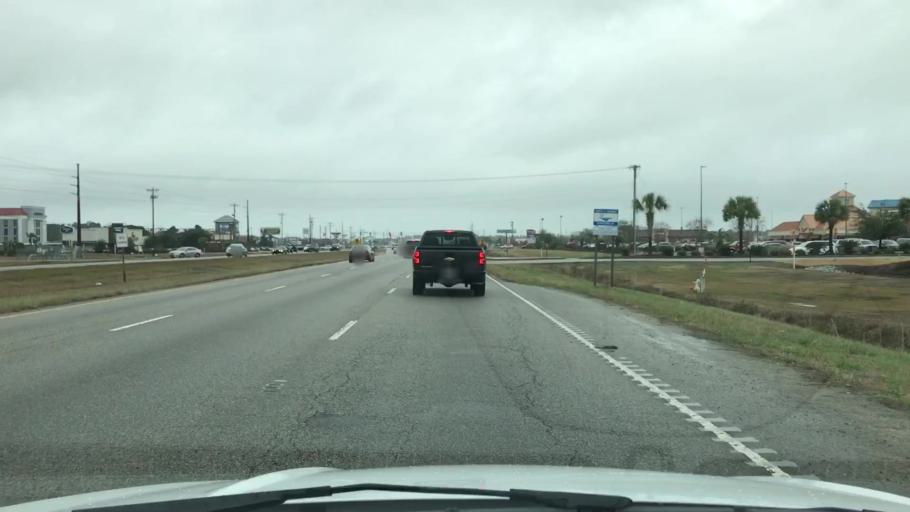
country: US
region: South Carolina
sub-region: Horry County
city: Forestbrook
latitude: 33.7501
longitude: -78.9601
